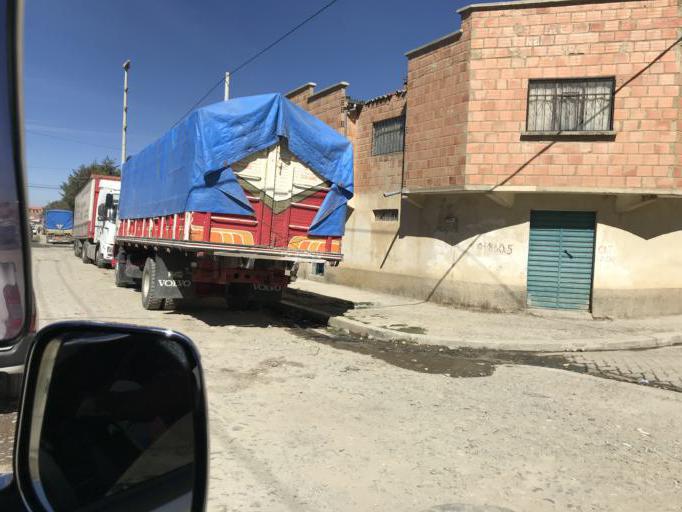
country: BO
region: La Paz
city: La Paz
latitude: -16.4867
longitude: -68.2107
